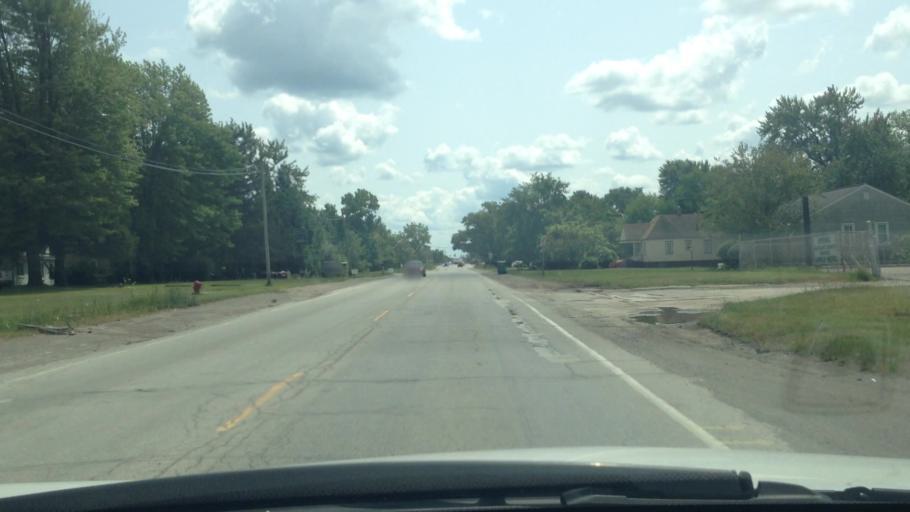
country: US
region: Michigan
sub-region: Wayne County
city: Inkster
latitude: 42.2588
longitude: -83.3087
